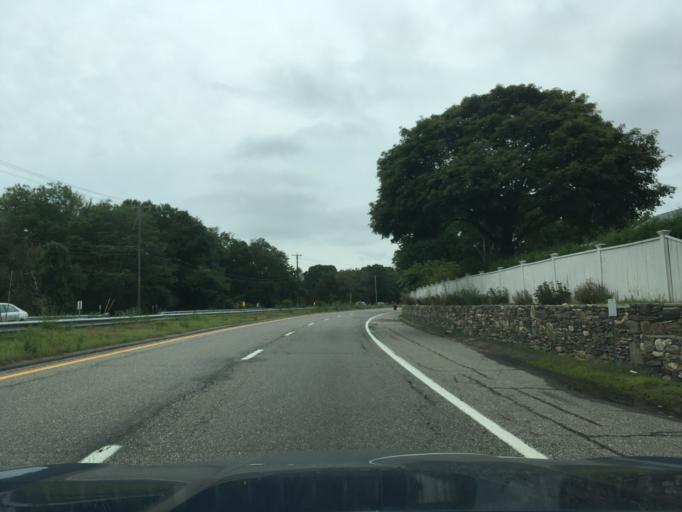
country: US
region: Rhode Island
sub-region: Bristol County
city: Barrington
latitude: 41.7623
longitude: -71.3215
